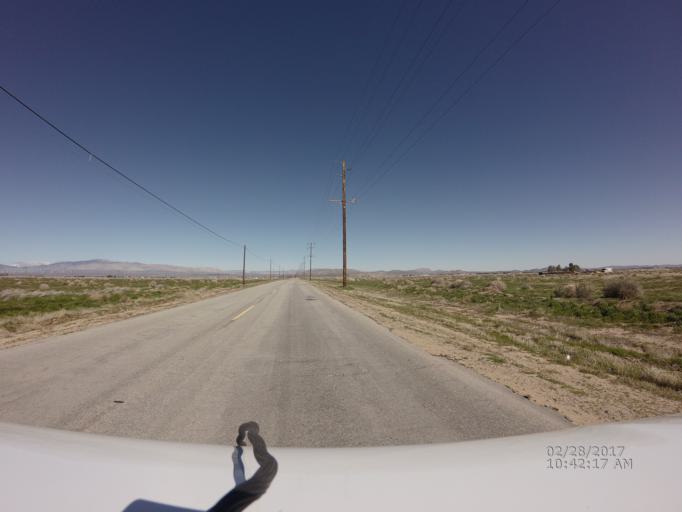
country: US
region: California
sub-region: Kern County
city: Rosamond
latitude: 34.8024
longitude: -118.2904
